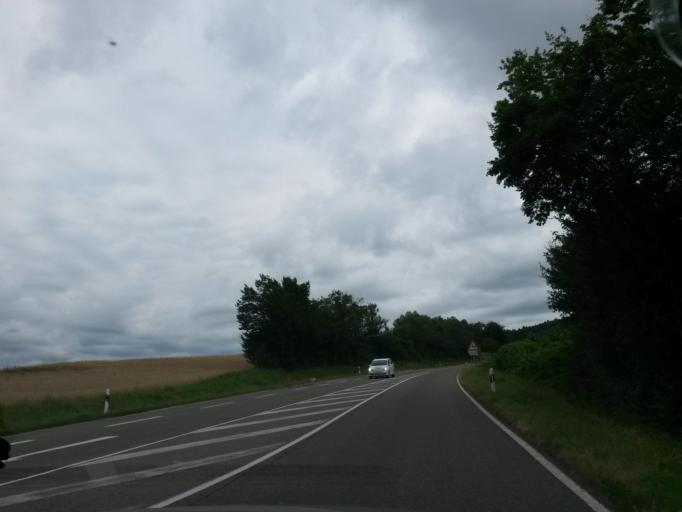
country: DE
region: Baden-Wuerttemberg
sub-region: Karlsruhe Region
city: Neuenburg
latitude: 48.8962
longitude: 8.5501
